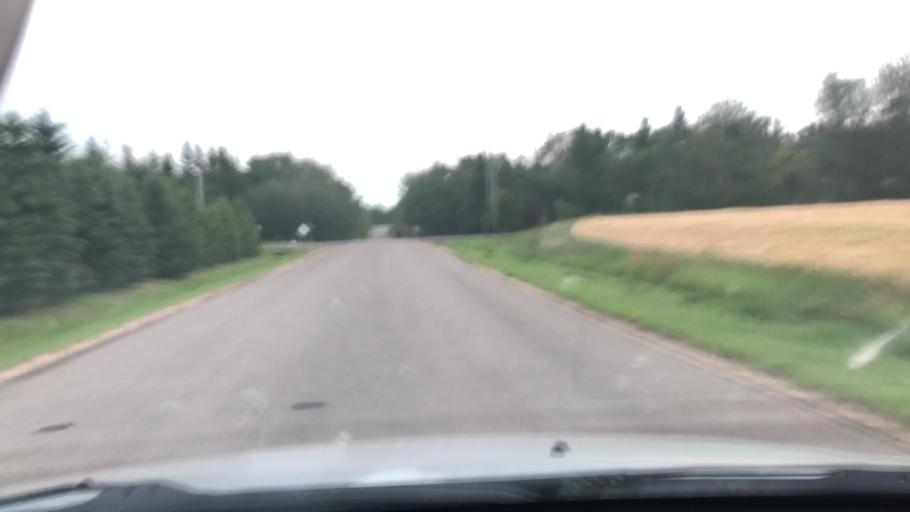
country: CA
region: Alberta
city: Devon
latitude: 53.4293
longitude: -113.6769
